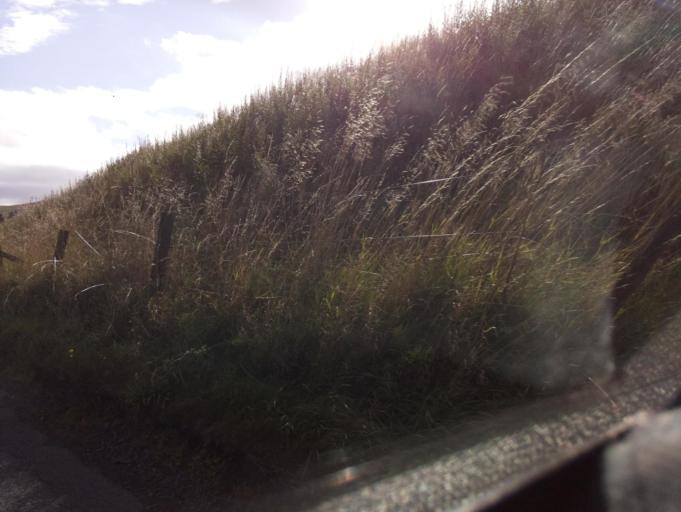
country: GB
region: Scotland
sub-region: South Lanarkshire
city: Biggar
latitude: 55.6399
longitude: -3.4258
